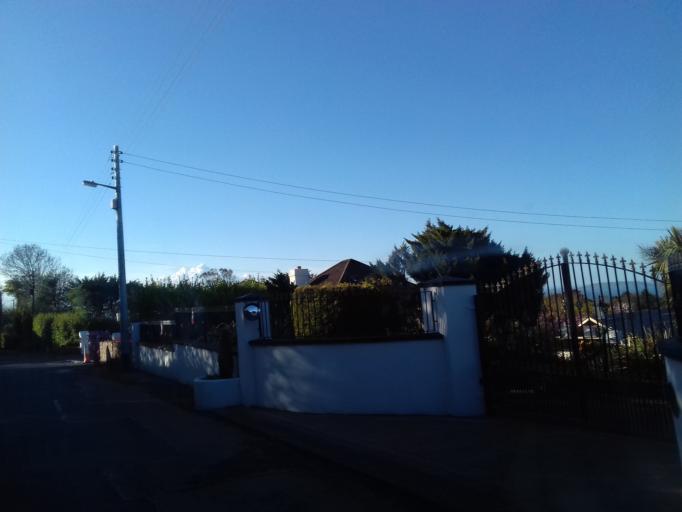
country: IE
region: Leinster
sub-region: Fingal County
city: Howth
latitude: 53.3763
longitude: -6.0628
